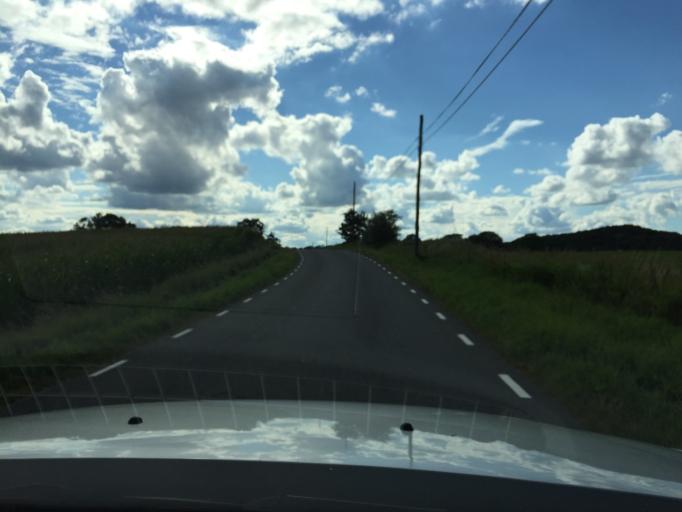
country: SE
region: Skane
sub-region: Hassleholms Kommun
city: Sosdala
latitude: 55.9910
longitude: 13.7314
